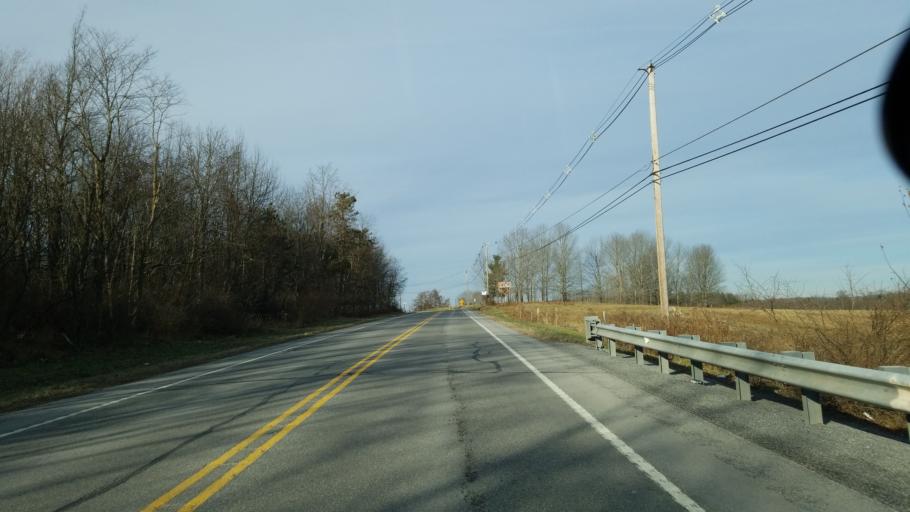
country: US
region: Pennsylvania
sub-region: Clearfield County
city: Curwensville
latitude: 40.9861
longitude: -78.6260
